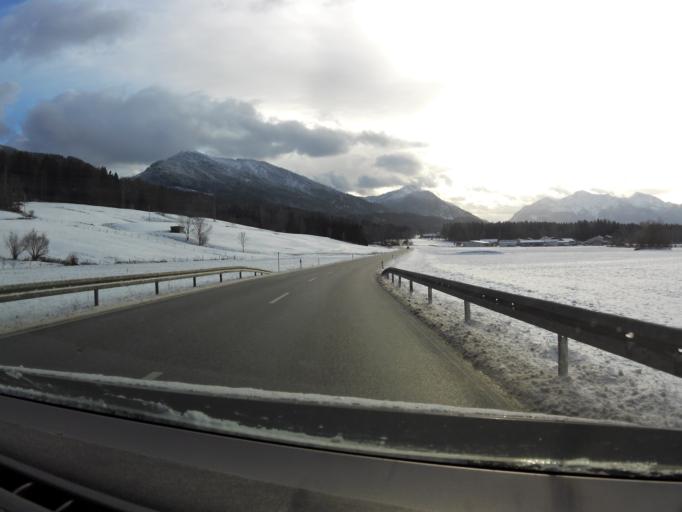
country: DE
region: Bavaria
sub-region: Upper Bavaria
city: Benediktbeuern
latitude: 47.6900
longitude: 11.4060
